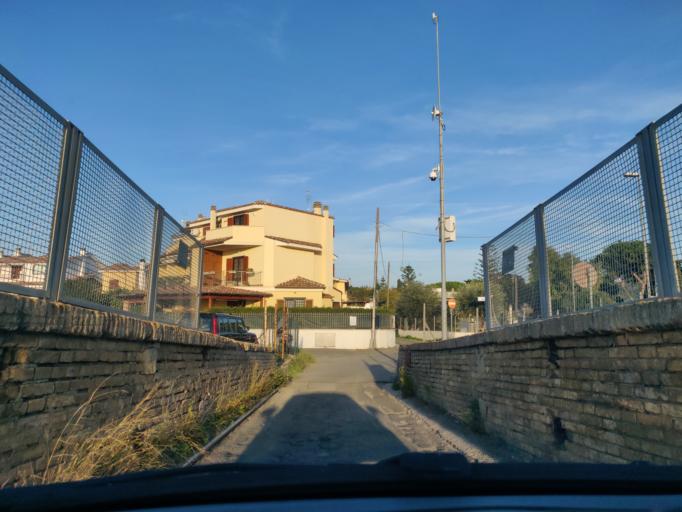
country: IT
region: Latium
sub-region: Citta metropolitana di Roma Capitale
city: Civitavecchia
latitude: 42.0619
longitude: 11.8179
